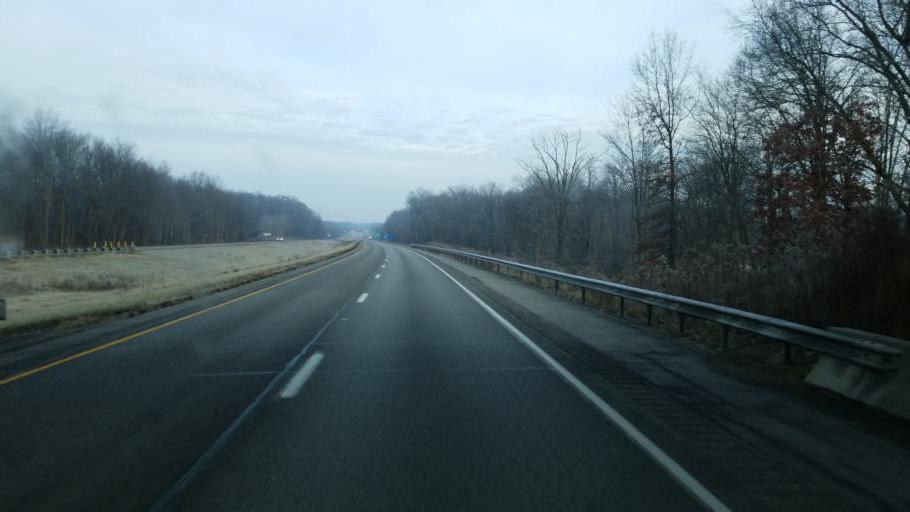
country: US
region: Pennsylvania
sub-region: Mercer County
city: Mercer
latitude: 41.2419
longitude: -80.1603
